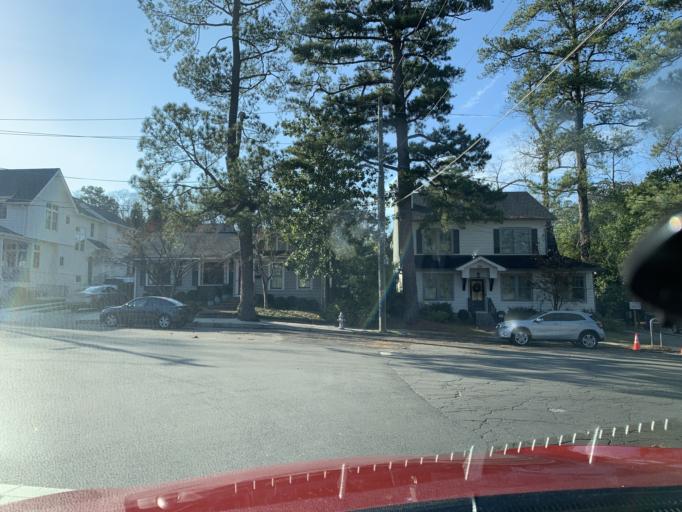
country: US
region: Georgia
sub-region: DeKalb County
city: Druid Hills
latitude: 33.7994
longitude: -84.3775
